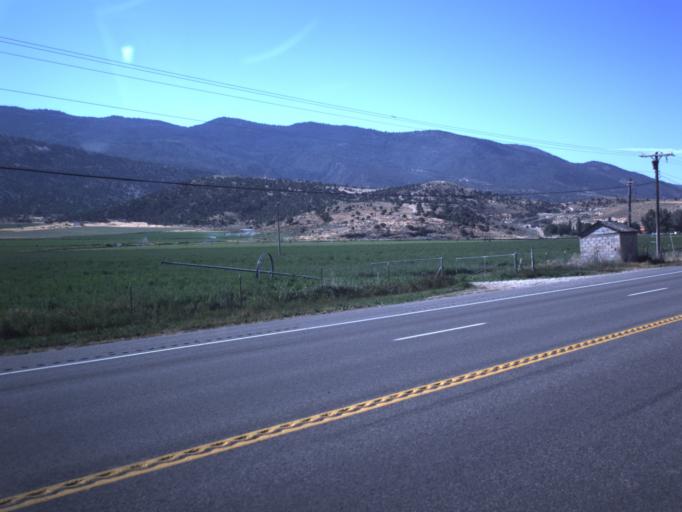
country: US
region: Utah
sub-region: Sanpete County
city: Manti
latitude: 39.2857
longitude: -111.6274
